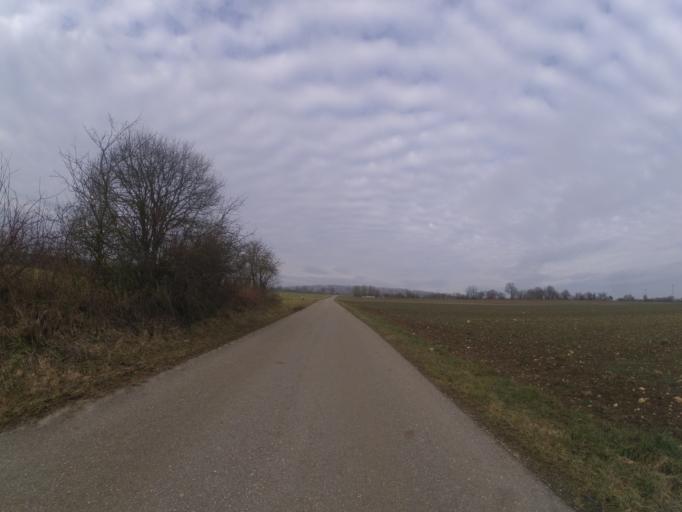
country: DE
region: Baden-Wuerttemberg
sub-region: Tuebingen Region
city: Mehrstetten
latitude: 48.3539
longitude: 9.5179
